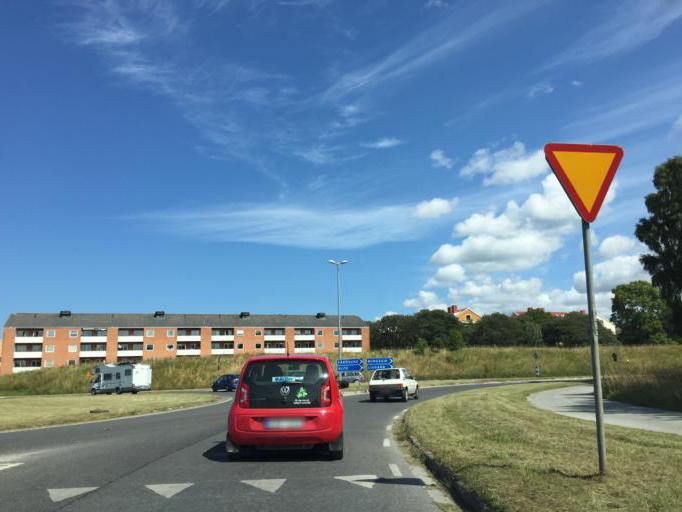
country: SE
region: Gotland
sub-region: Gotland
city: Visby
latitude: 57.6215
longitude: 18.2769
